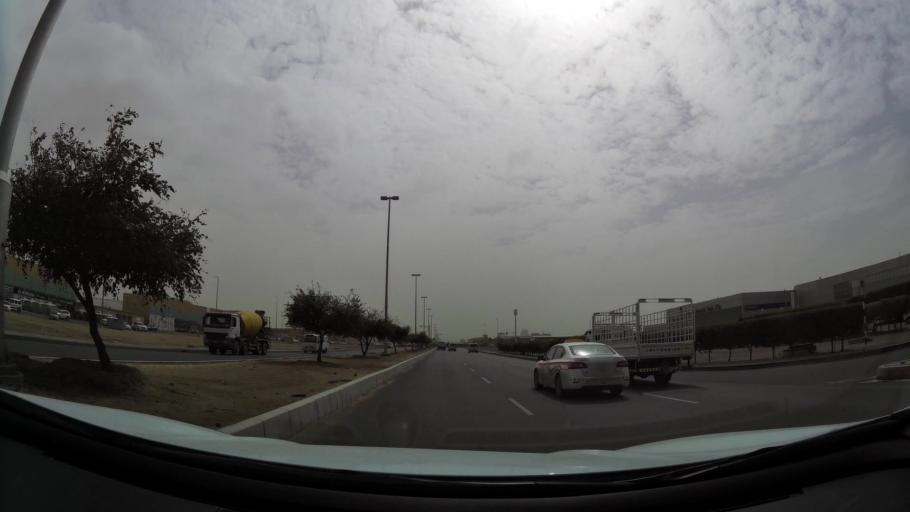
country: AE
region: Abu Dhabi
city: Abu Dhabi
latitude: 24.3467
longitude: 54.4727
